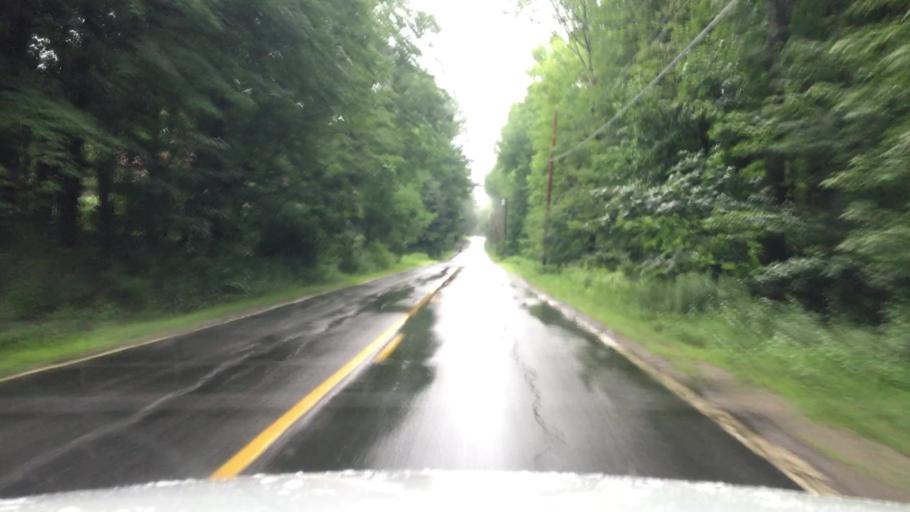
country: US
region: Maine
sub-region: Kennebec County
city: Winthrop
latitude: 44.2942
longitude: -69.9288
